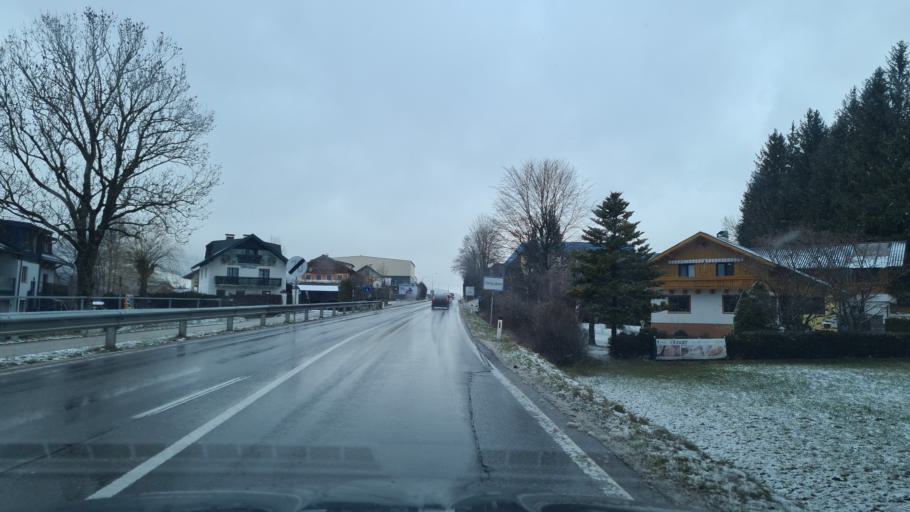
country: AT
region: Upper Austria
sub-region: Politischer Bezirk Vocklabruck
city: Mondsee
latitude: 47.8691
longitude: 13.3254
